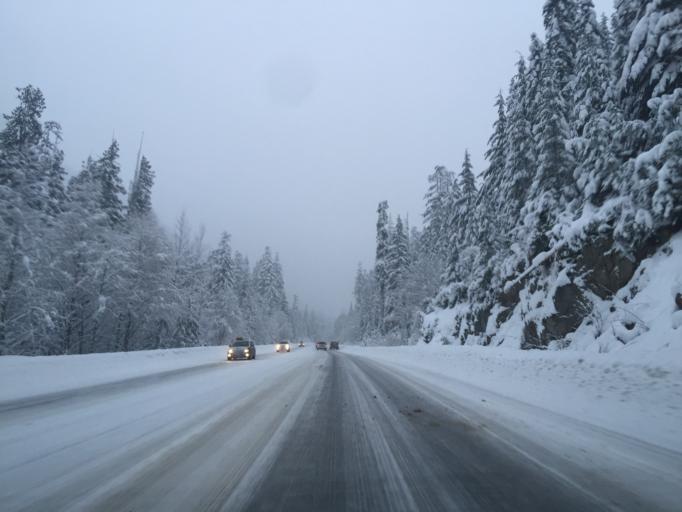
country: US
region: Washington
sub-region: Chelan County
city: Leavenworth
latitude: 47.7149
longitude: -121.1380
